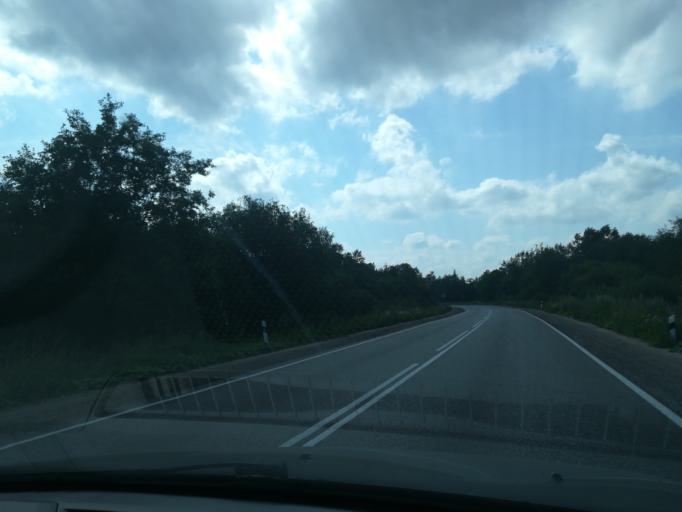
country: RU
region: Leningrad
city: Kopor'ye
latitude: 59.6740
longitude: 29.0278
